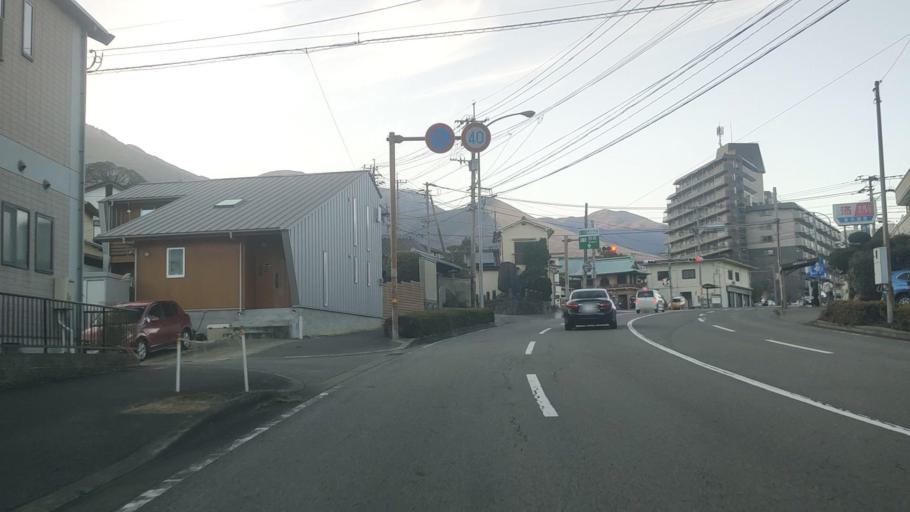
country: JP
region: Oita
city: Beppu
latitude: 33.2863
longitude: 131.4743
